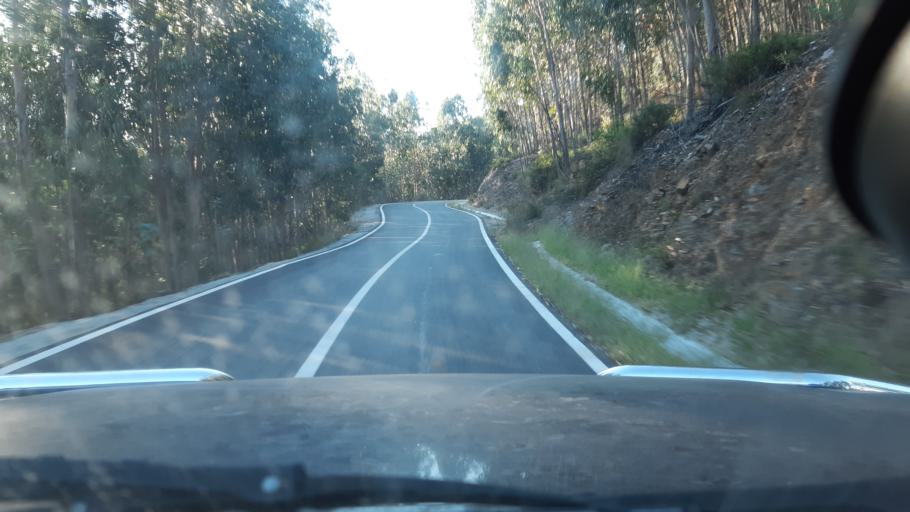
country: PT
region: Viseu
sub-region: Mortagua
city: Mortagua
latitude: 40.5377
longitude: -8.2459
